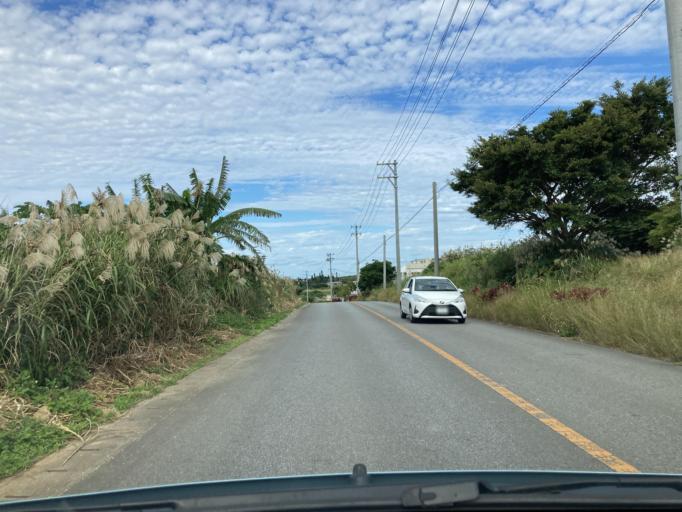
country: JP
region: Okinawa
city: Ishikawa
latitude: 26.4306
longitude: 127.7286
